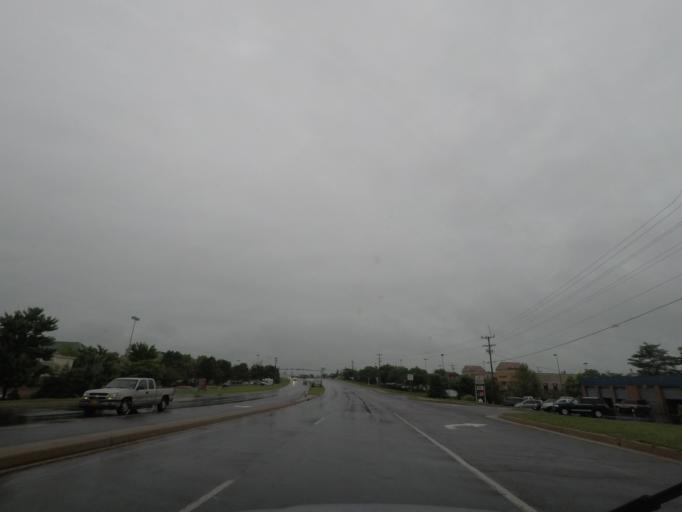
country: US
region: Virginia
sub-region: Culpeper County
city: Culpeper
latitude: 38.4858
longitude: -77.9668
